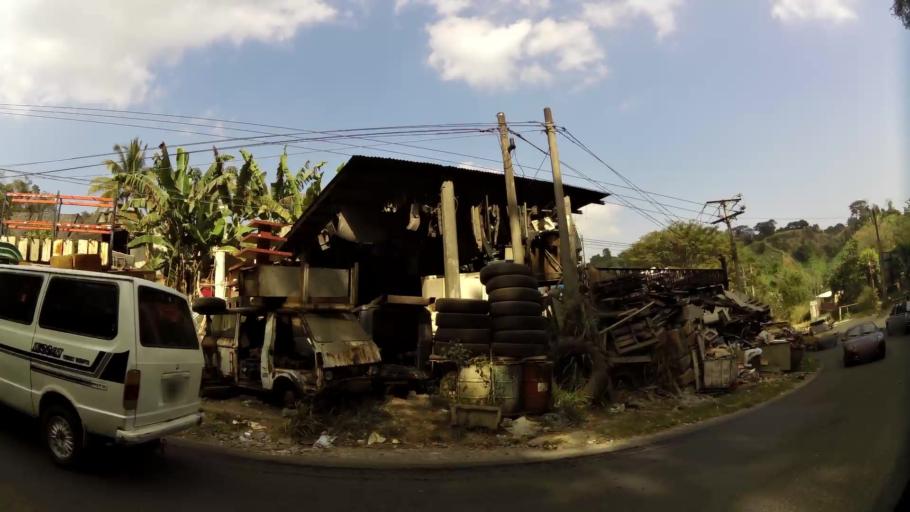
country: SV
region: San Salvador
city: Delgado
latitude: 13.7167
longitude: -89.1623
